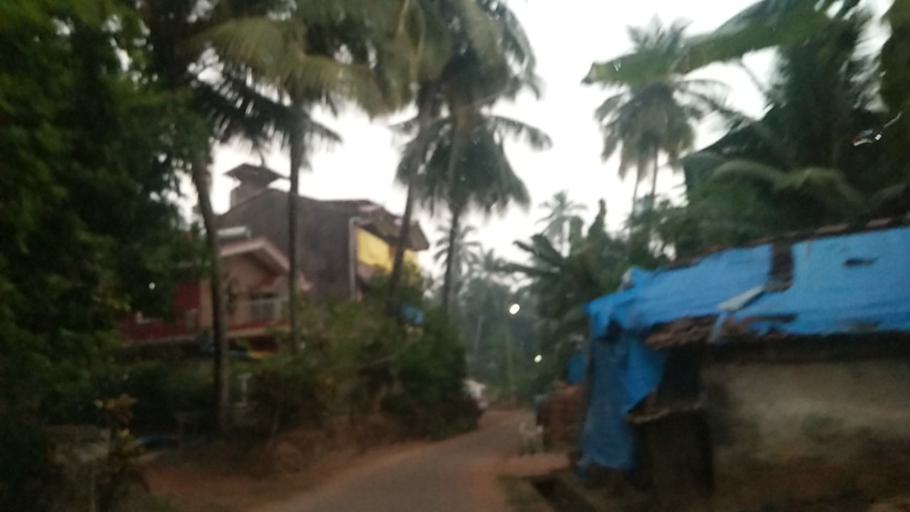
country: IN
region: Goa
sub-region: South Goa
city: Madgaon
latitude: 15.2849
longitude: 73.9549
